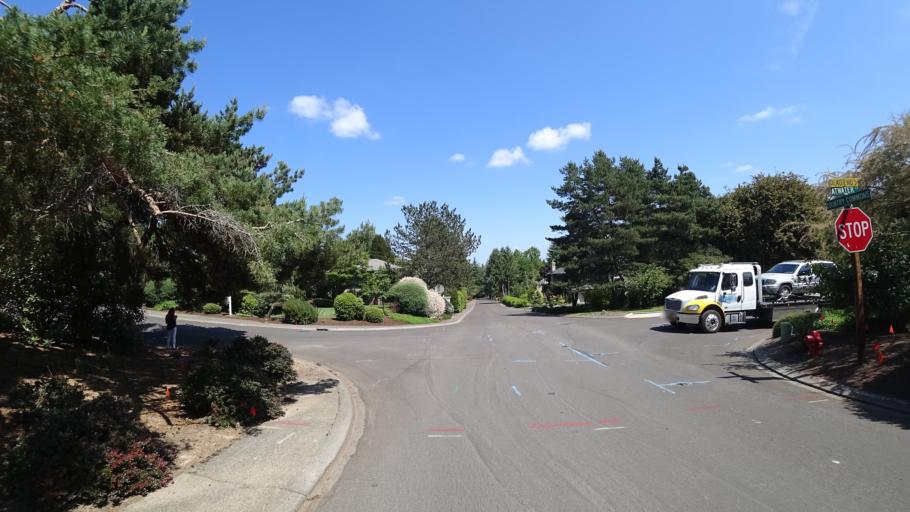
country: US
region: Oregon
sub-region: Clackamas County
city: Lake Oswego
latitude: 45.4286
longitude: -122.6889
